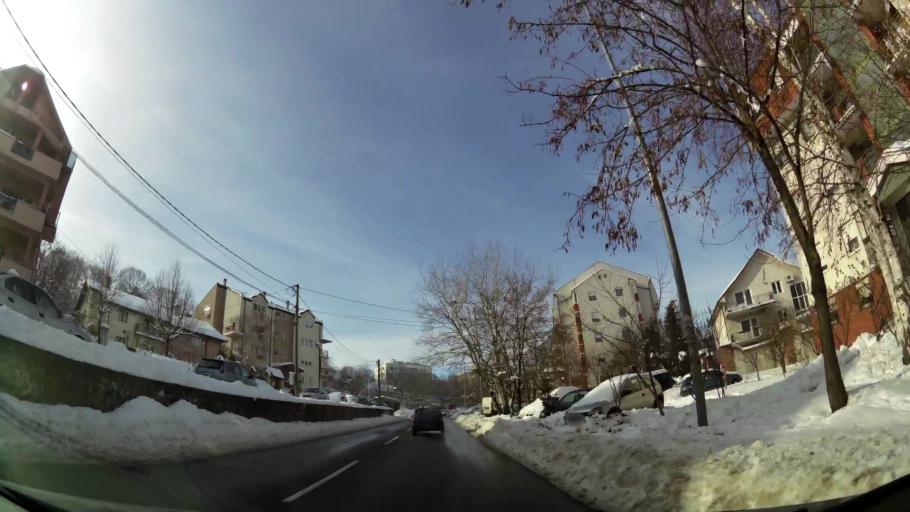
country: RS
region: Central Serbia
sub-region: Belgrade
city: Zvezdara
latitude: 44.7909
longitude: 20.5210
